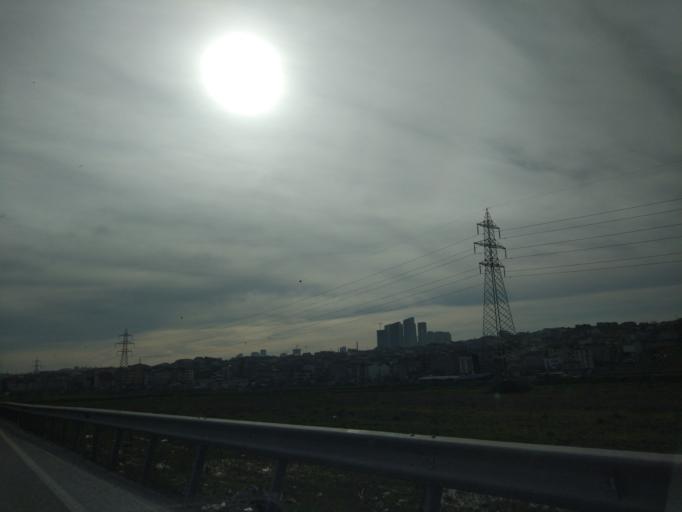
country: TR
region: Istanbul
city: Esenyurt
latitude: 41.0488
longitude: 28.7024
